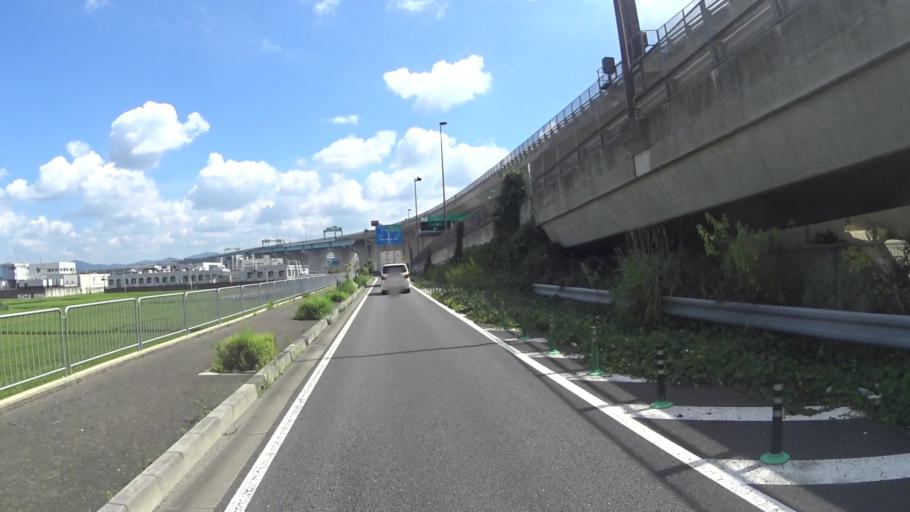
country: JP
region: Kyoto
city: Yawata
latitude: 34.8992
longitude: 135.7404
